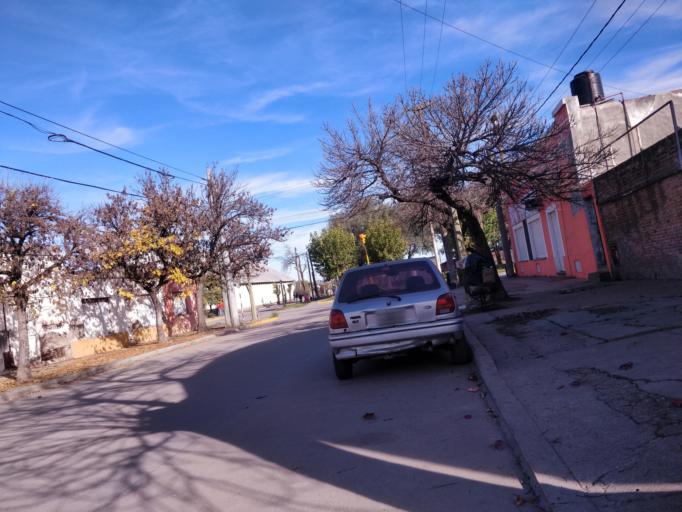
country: AR
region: Cordoba
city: Leones
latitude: -32.6640
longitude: -62.2949
